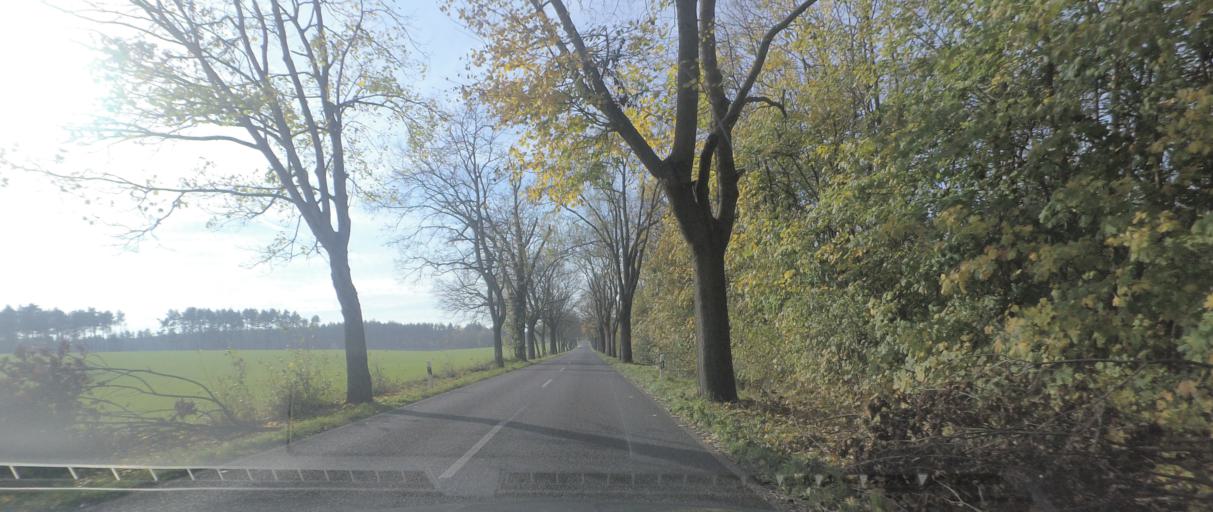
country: DE
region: Brandenburg
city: Am Mellensee
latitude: 52.1541
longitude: 13.3942
